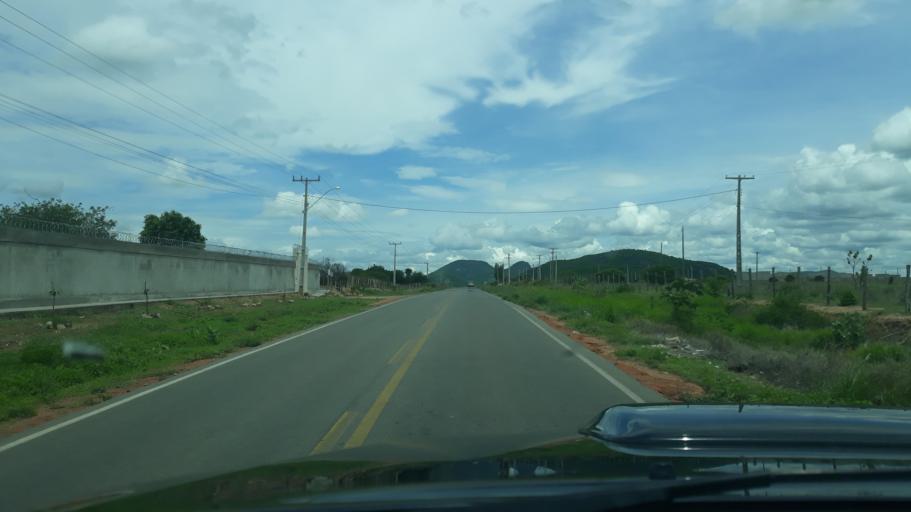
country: BR
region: Bahia
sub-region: Guanambi
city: Guanambi
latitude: -14.2484
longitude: -42.7521
